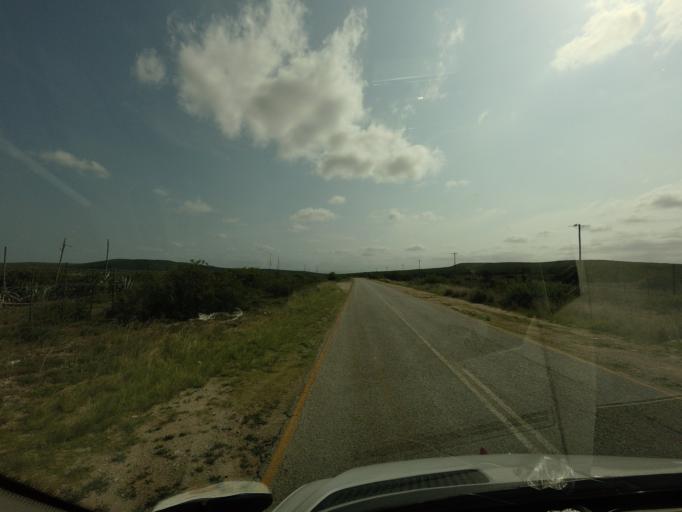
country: ZA
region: Eastern Cape
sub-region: Nelson Mandela Bay Metropolitan Municipality
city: Uitenhage
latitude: -33.6263
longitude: 25.6049
